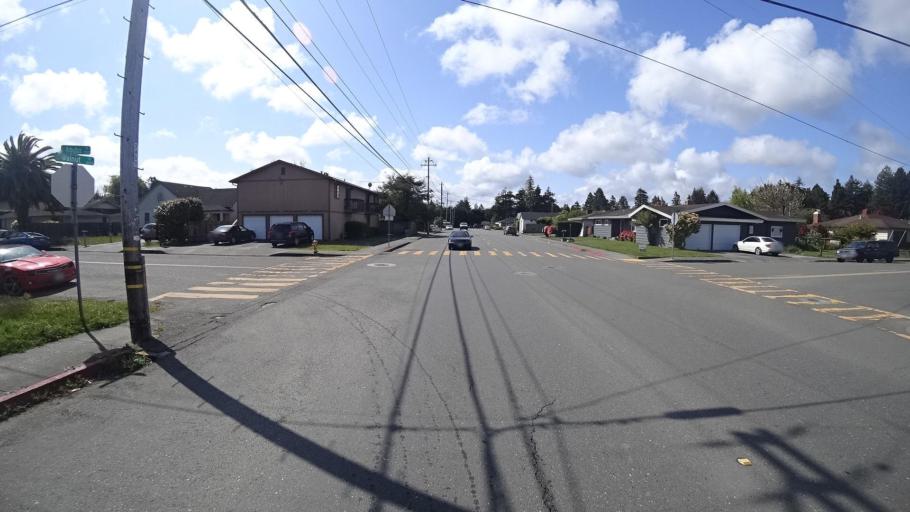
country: US
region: California
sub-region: Humboldt County
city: Cutten
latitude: 40.7679
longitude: -124.1430
